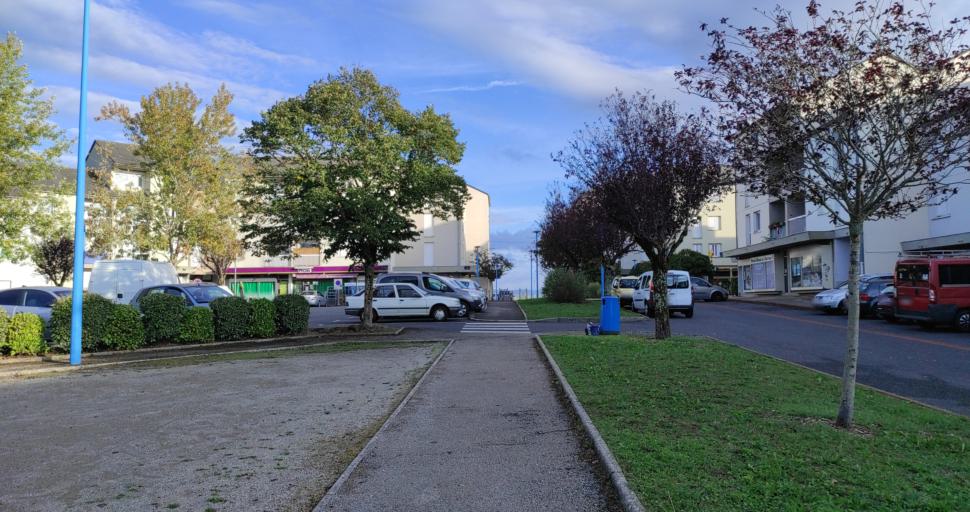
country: FR
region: Midi-Pyrenees
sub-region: Departement de l'Aveyron
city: Rodez
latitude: 44.3767
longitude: 2.5705
